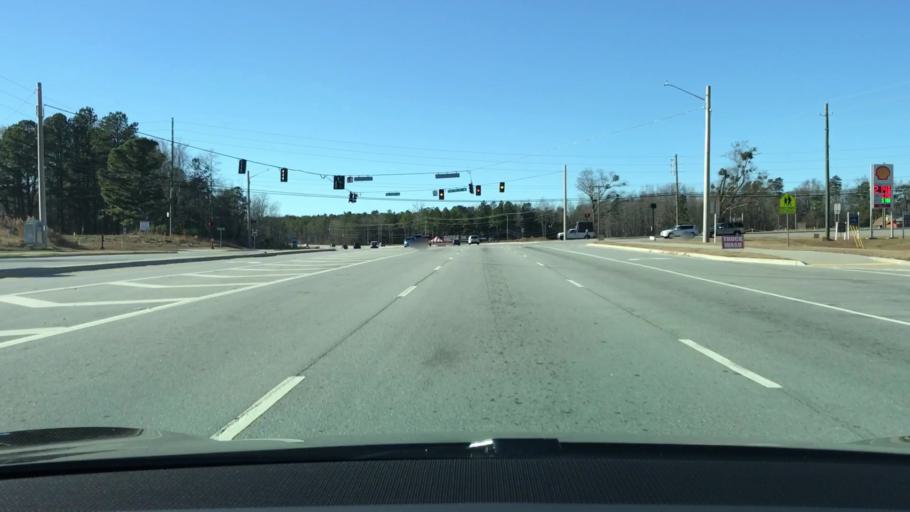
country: US
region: Georgia
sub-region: Hall County
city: Flowery Branch
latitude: 34.1334
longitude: -83.9342
